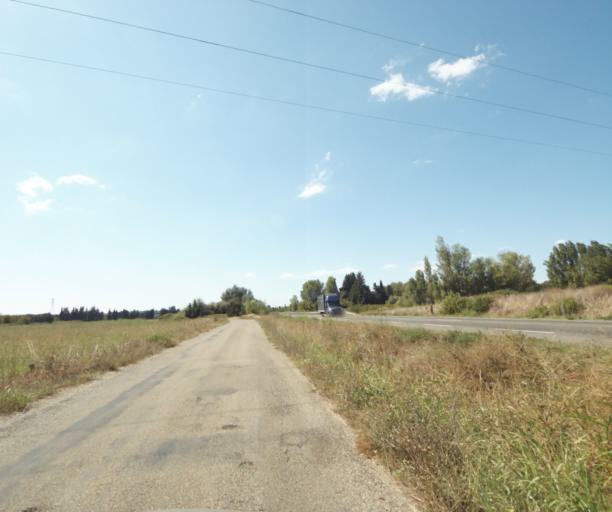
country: FR
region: Languedoc-Roussillon
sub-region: Departement du Gard
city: Rodilhan
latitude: 43.8174
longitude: 4.4153
